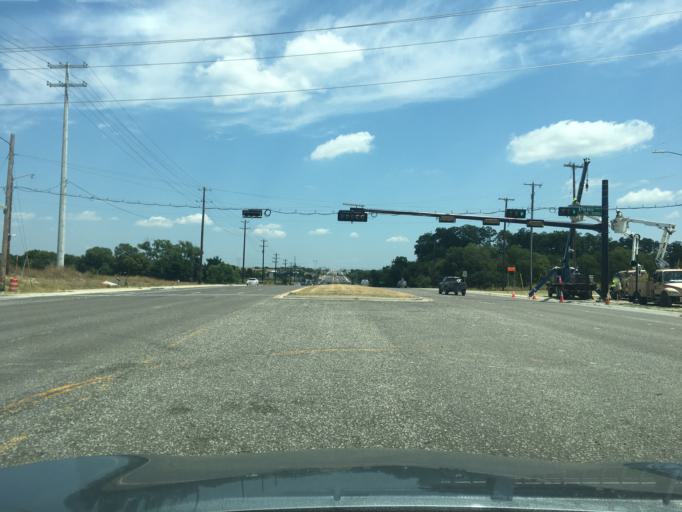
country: US
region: Texas
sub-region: Collin County
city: Prosper
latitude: 33.2189
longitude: -96.7940
